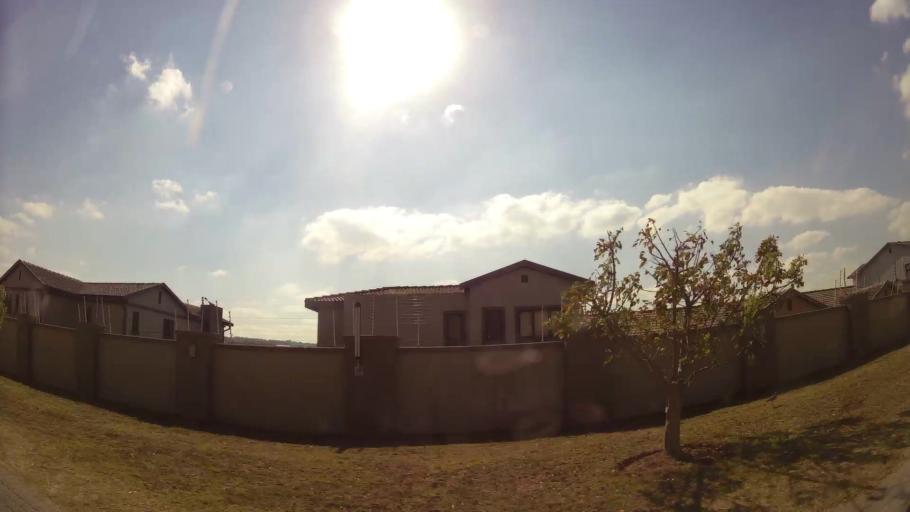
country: ZA
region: Gauteng
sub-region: City of Johannesburg Metropolitan Municipality
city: Midrand
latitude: -26.0080
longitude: 28.0745
